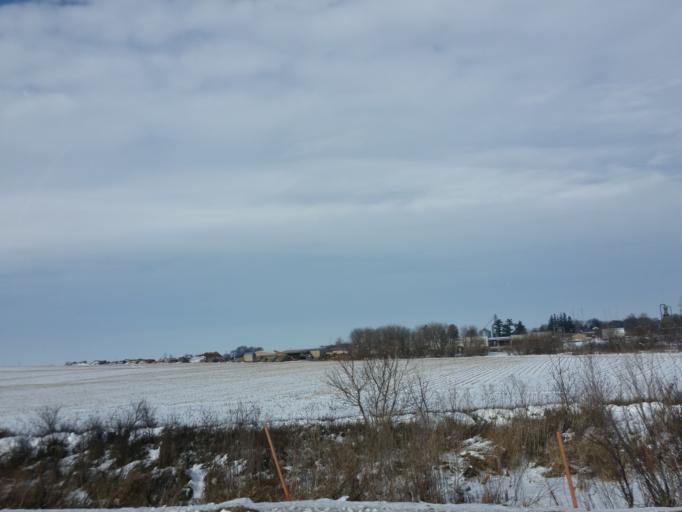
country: US
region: Iowa
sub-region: Buchanan County
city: Independence
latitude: 42.4617
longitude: -91.7402
